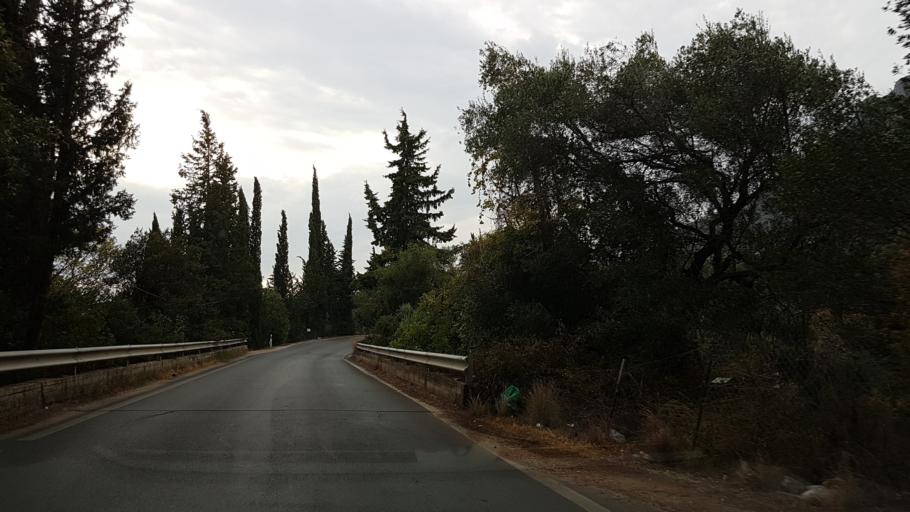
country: GR
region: Ionian Islands
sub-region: Nomos Kerkyras
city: Kontokali
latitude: 39.7244
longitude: 19.8887
